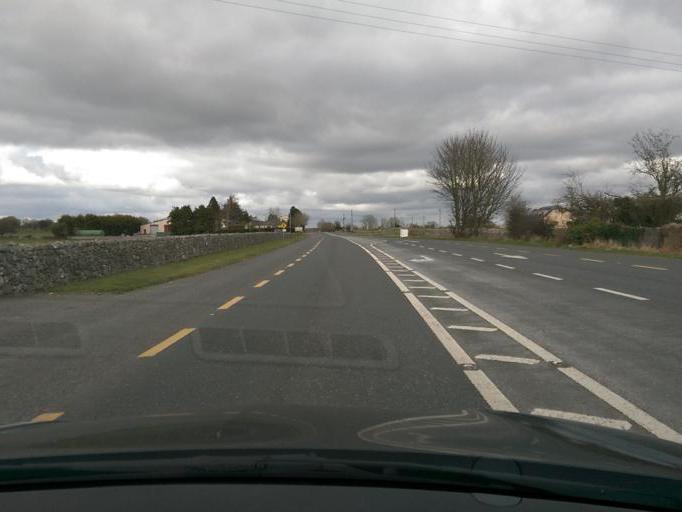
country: IE
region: Connaught
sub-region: County Galway
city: Ballinasloe
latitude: 53.3476
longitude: -8.0887
